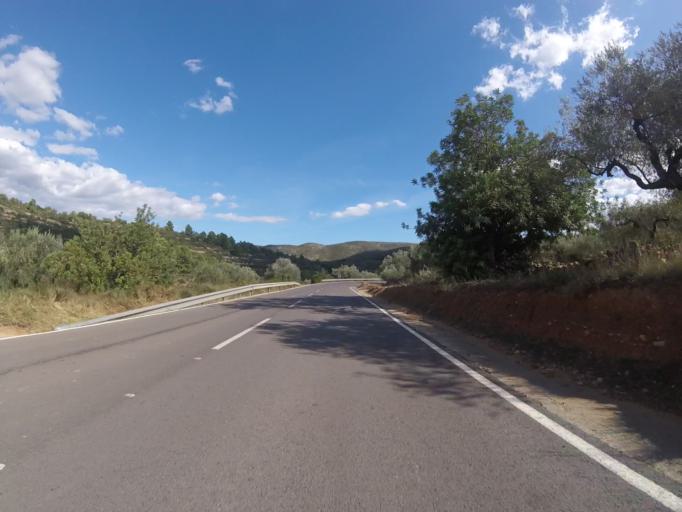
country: ES
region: Valencia
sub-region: Provincia de Castello
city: Cuevas de Vinroma
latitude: 40.3049
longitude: 0.1625
